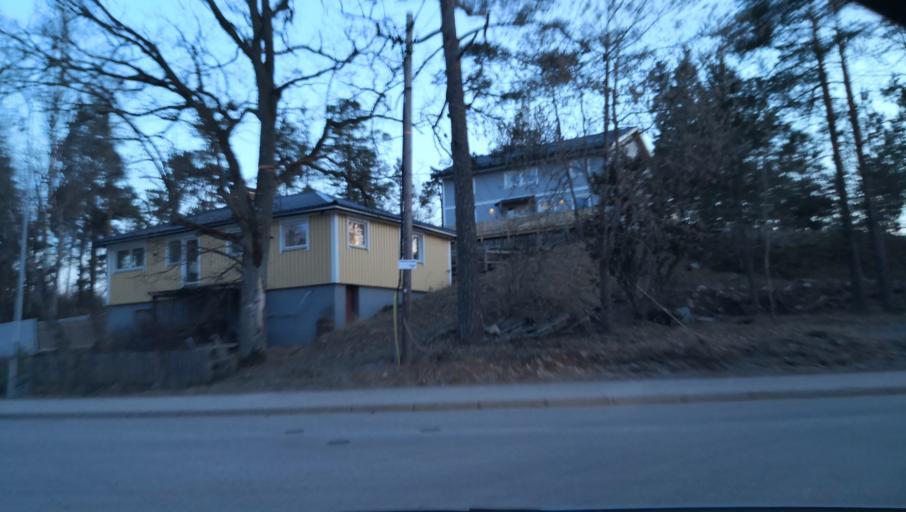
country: SE
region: Stockholm
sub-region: Nacka Kommun
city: Kummelnas
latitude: 59.3434
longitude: 18.2916
